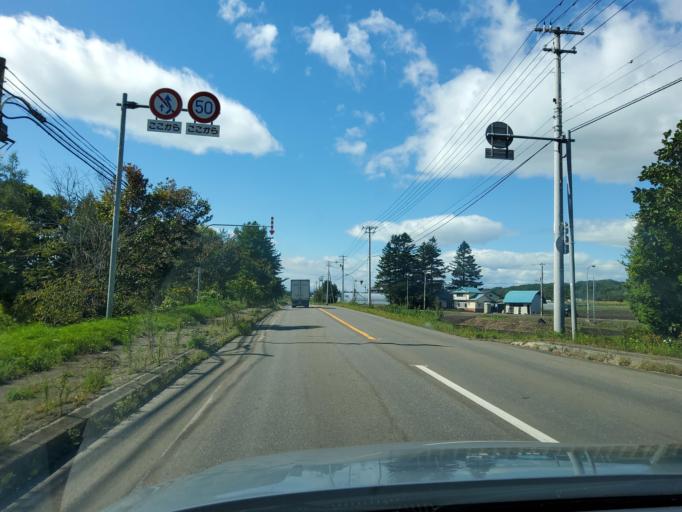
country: JP
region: Hokkaido
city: Obihiro
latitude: 42.9373
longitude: 143.2878
